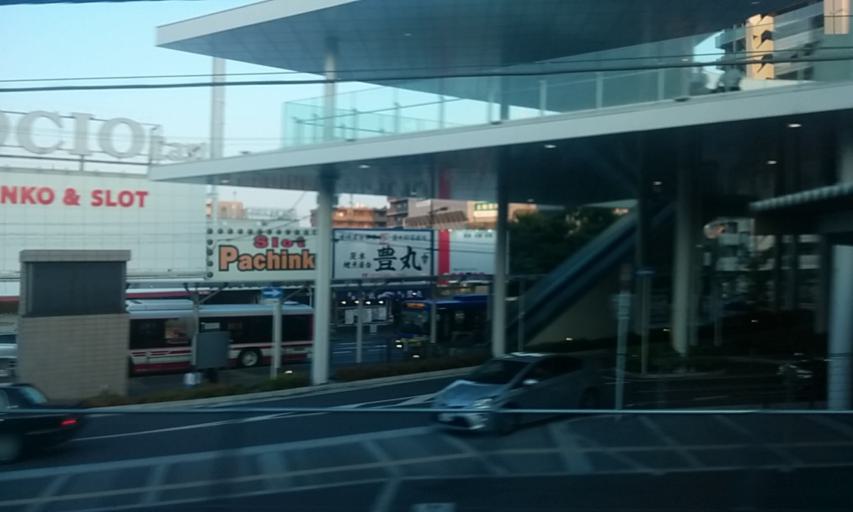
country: JP
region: Osaka
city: Ibaraki
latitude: 34.8156
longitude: 135.5627
